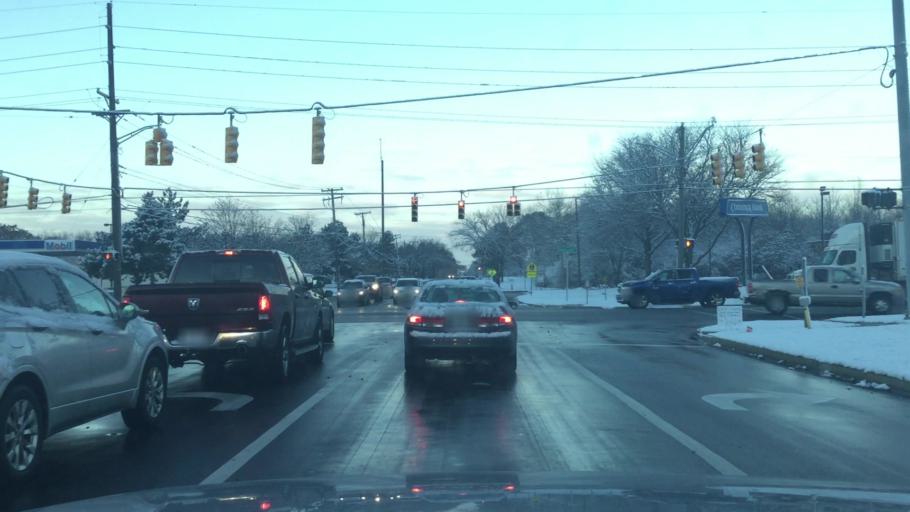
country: US
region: Michigan
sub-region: Oakland County
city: Wolverine Lake
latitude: 42.5926
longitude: -83.4455
